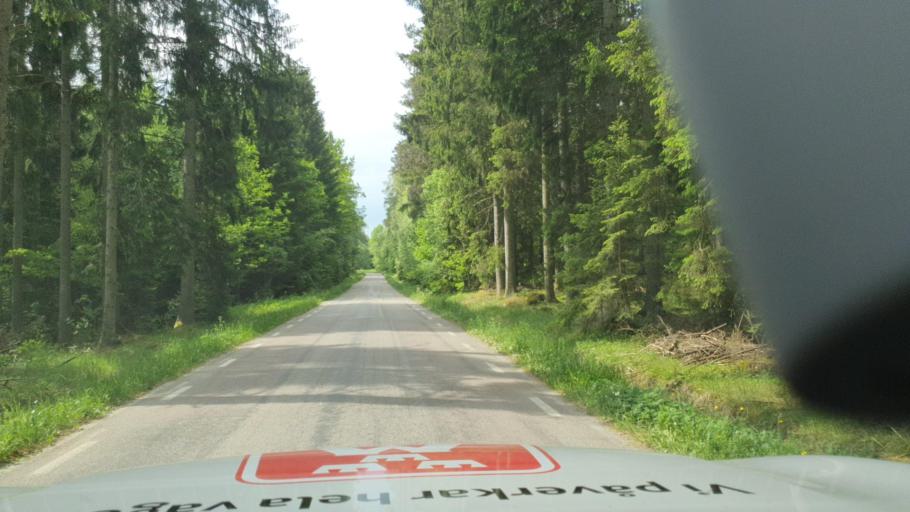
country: SE
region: Vaestra Goetaland
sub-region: Falkopings Kommun
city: Floby
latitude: 57.9730
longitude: 13.3971
